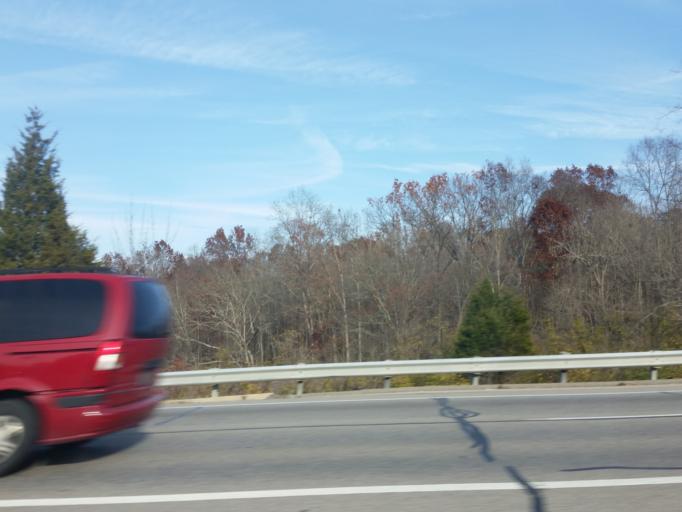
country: US
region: Kentucky
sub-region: Campbell County
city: Alexandria
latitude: 38.9916
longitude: -84.4090
